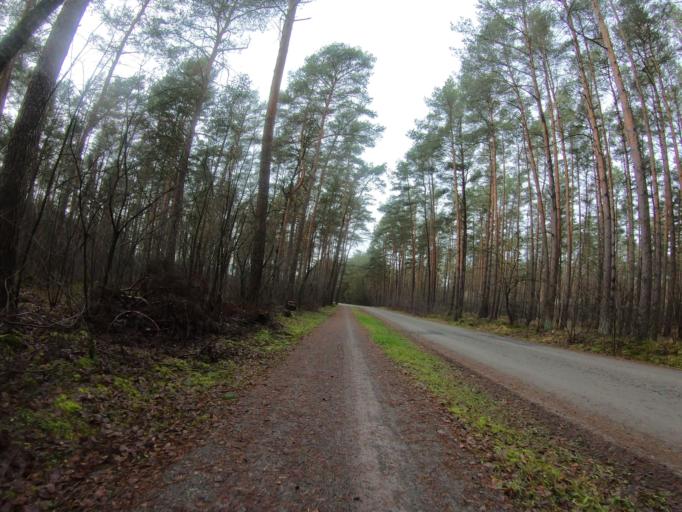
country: DE
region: Lower Saxony
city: Muden
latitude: 52.5095
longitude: 10.4245
